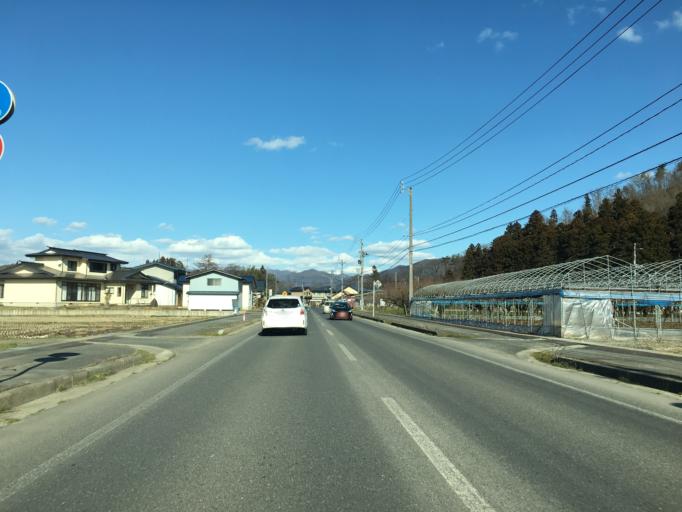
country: JP
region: Yamagata
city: Takahata
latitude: 37.9963
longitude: 140.1880
